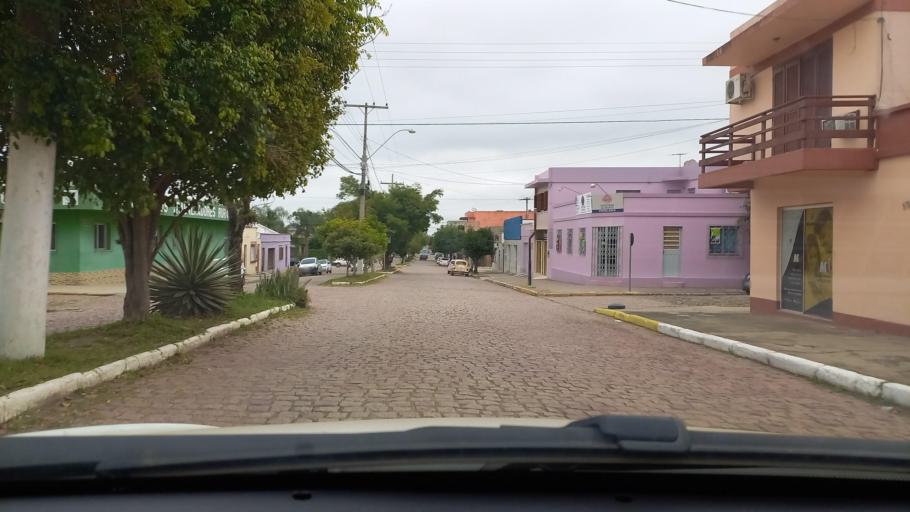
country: BR
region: Rio Grande do Sul
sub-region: Dom Pedrito
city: Dom Pedrito
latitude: -30.9798
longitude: -54.6691
